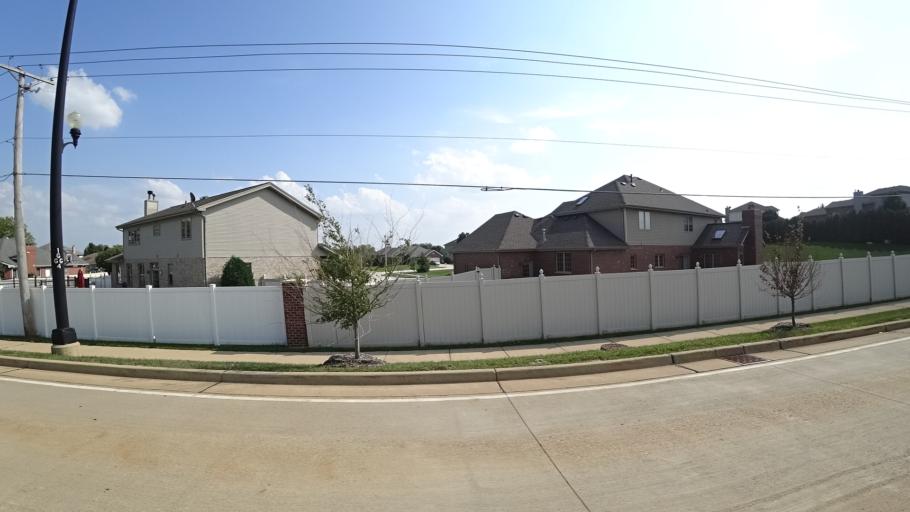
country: US
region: Illinois
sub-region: Cook County
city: Orland Hills
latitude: 41.5579
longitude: -87.8336
